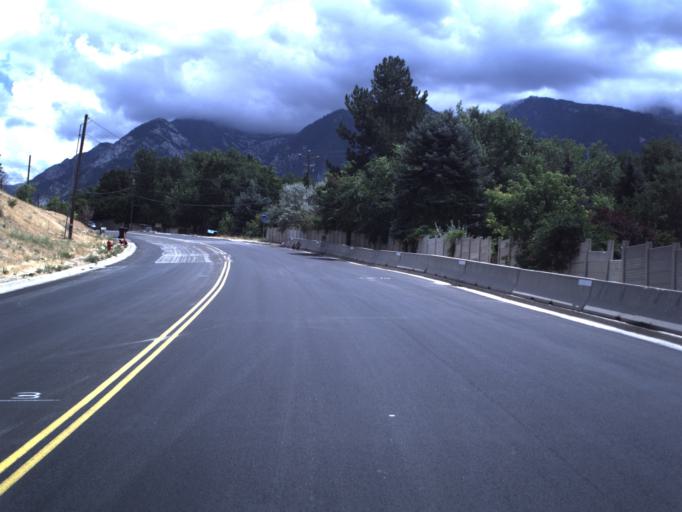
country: US
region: Utah
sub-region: Salt Lake County
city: Granite
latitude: 40.5771
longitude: -111.8210
